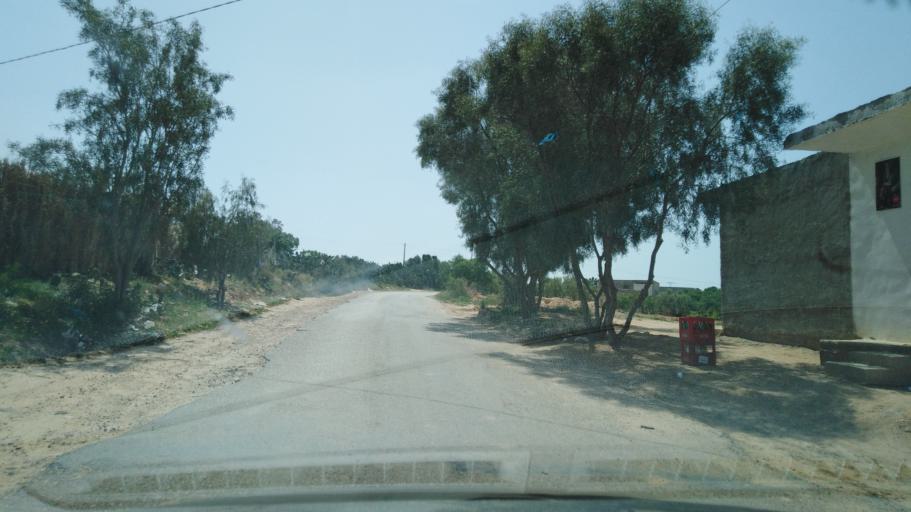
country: TN
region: Safaqis
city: Sfax
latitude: 34.7202
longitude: 10.5315
